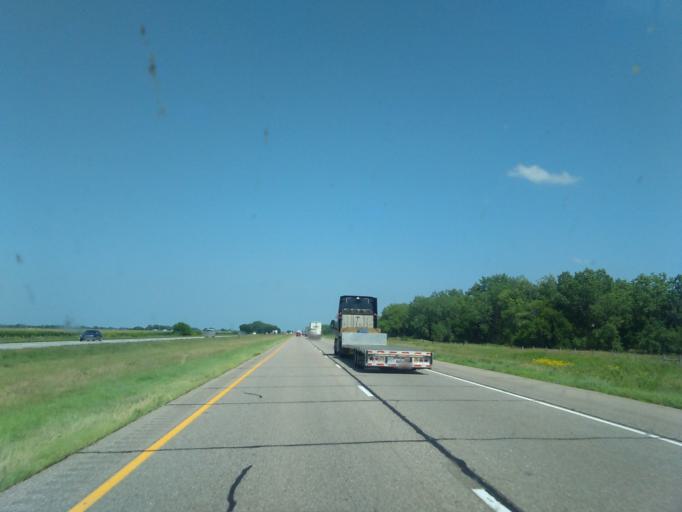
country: US
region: Nebraska
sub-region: Buffalo County
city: Kearney
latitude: 40.6722
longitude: -99.2120
